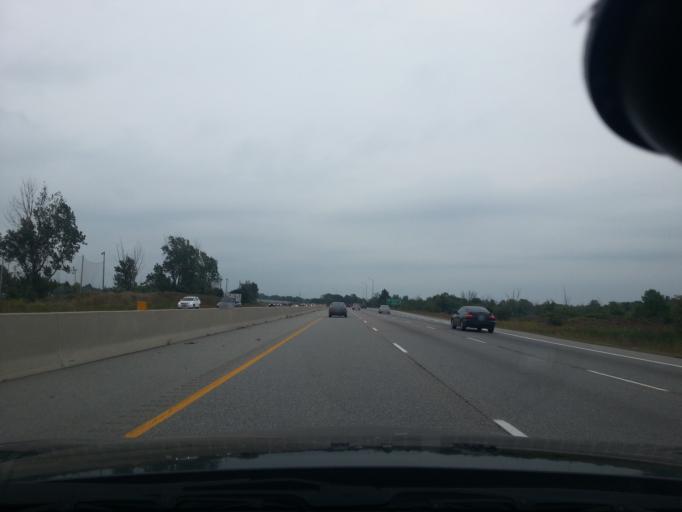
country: CA
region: Ontario
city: Kingston
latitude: 44.2791
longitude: -76.5526
